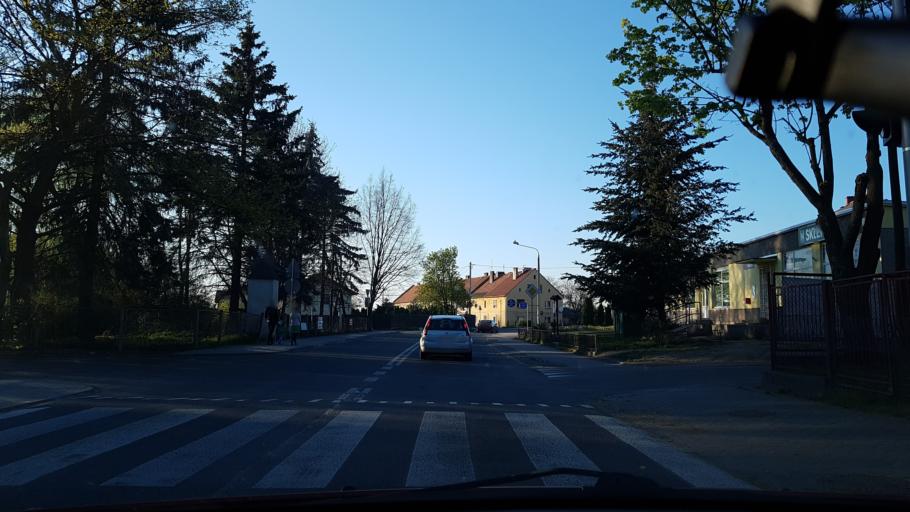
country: PL
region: Opole Voivodeship
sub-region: Powiat nyski
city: Nysa
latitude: 50.4342
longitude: 17.3057
